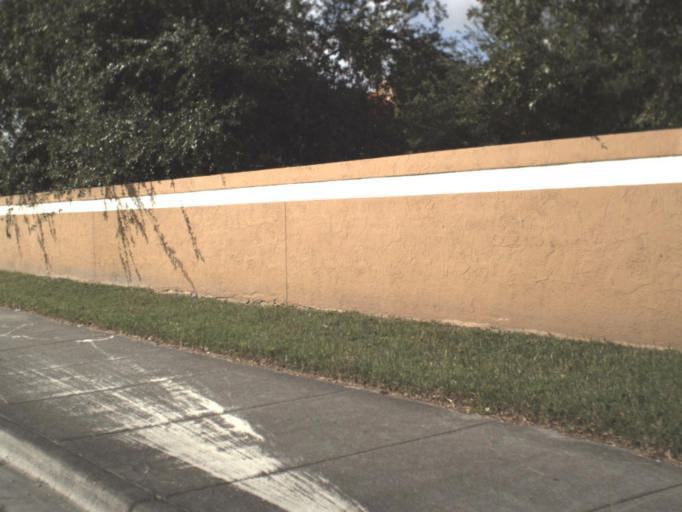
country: US
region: Florida
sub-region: Miami-Dade County
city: Three Lakes
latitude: 25.6271
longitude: -80.3909
